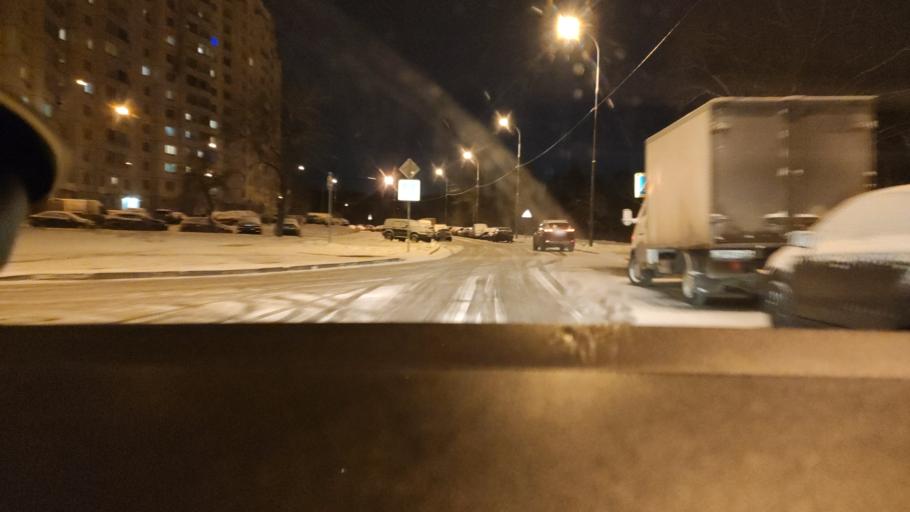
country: RU
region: Moscow
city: Annino
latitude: 55.5499
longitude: 37.5725
